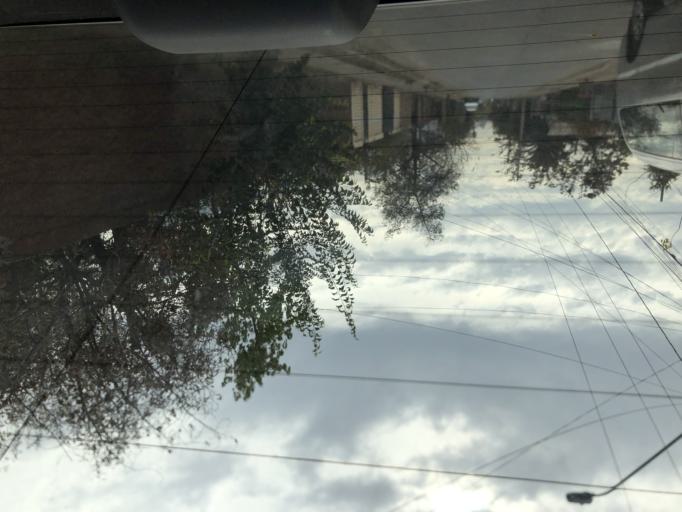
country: CL
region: Santiago Metropolitan
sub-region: Provincia de Cordillera
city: Puente Alto
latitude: -33.6106
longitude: -70.5320
